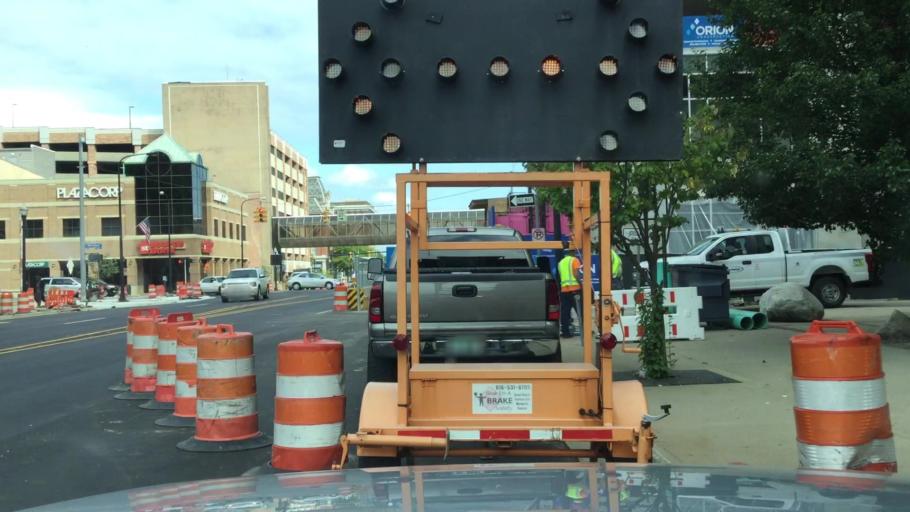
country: US
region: Michigan
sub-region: Kalamazoo County
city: Kalamazoo
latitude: 42.2909
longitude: -85.5846
